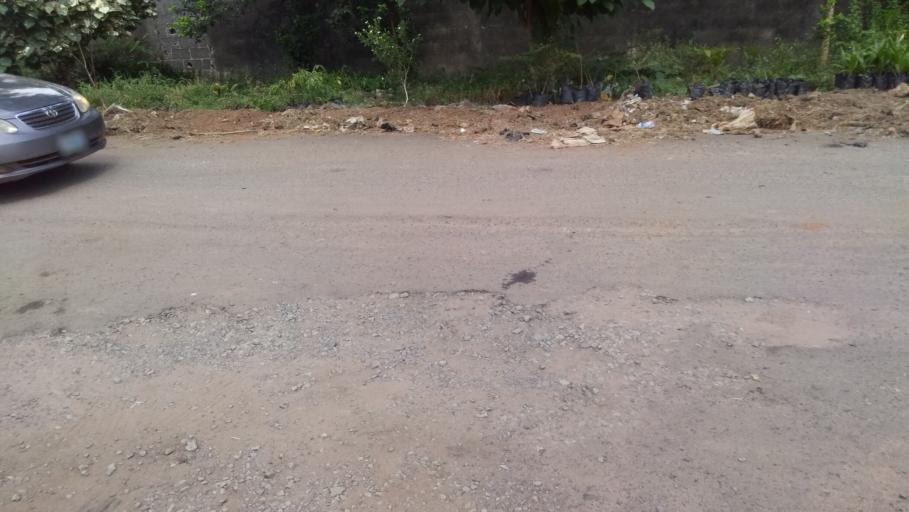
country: NG
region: Imo
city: Owerri
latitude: 5.4717
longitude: 7.0198
